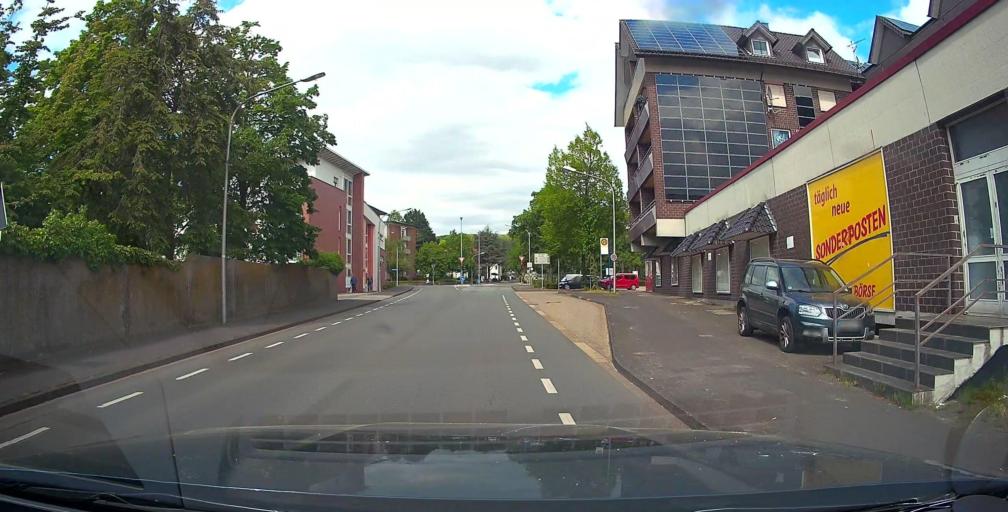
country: DE
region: North Rhine-Westphalia
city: Lengerich
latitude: 52.1900
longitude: 7.8480
